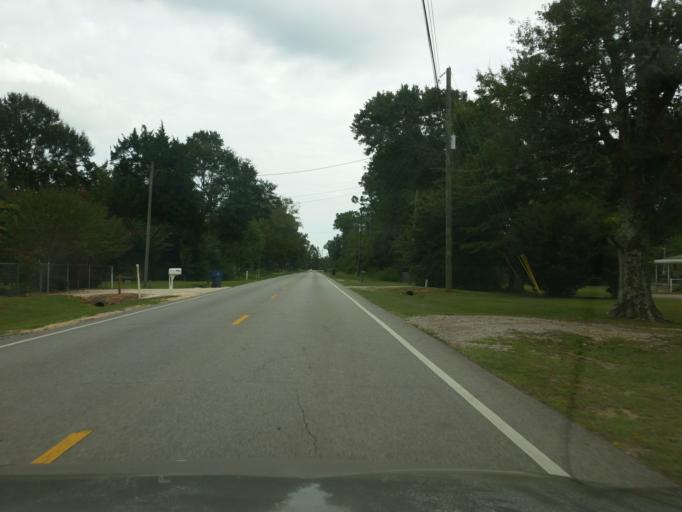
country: US
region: Florida
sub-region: Escambia County
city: Molino
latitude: 30.6831
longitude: -87.3229
